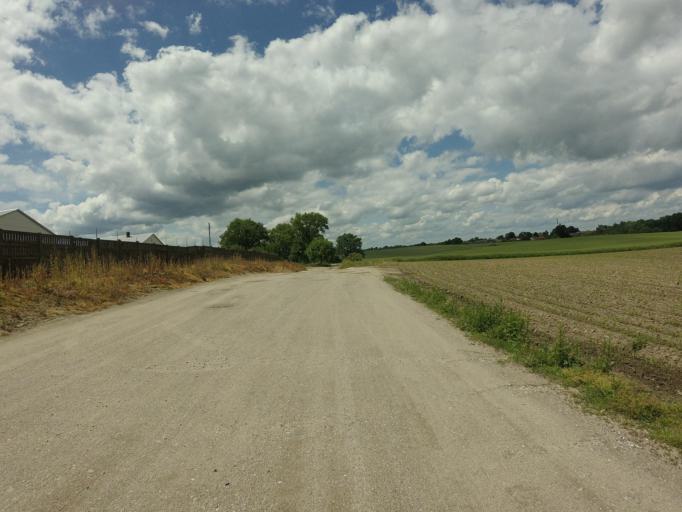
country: PL
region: West Pomeranian Voivodeship
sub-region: Powiat choszczenski
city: Krzecin
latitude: 52.9978
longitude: 15.4305
